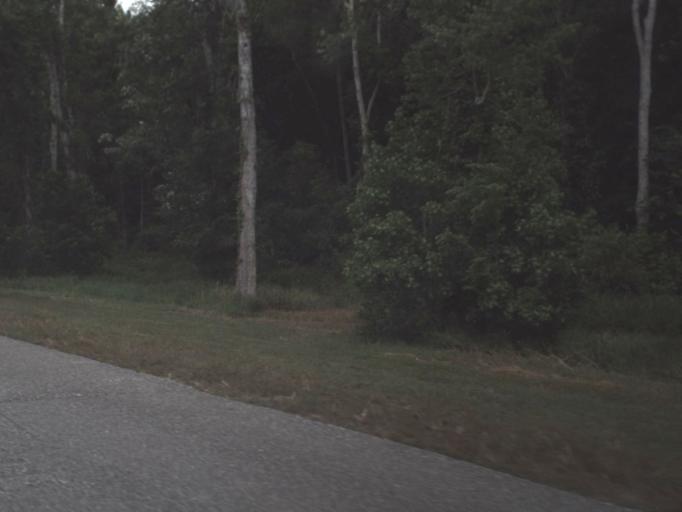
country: US
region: Florida
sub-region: Orange County
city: Wedgefield
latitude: 28.4526
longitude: -81.0007
